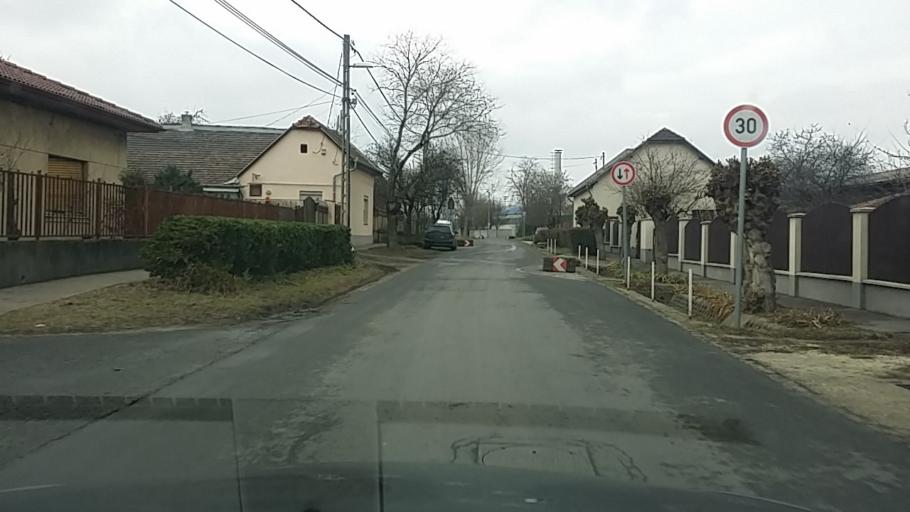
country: HU
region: Budapest
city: Budapest XXII. keruelet
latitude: 47.4120
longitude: 19.0535
